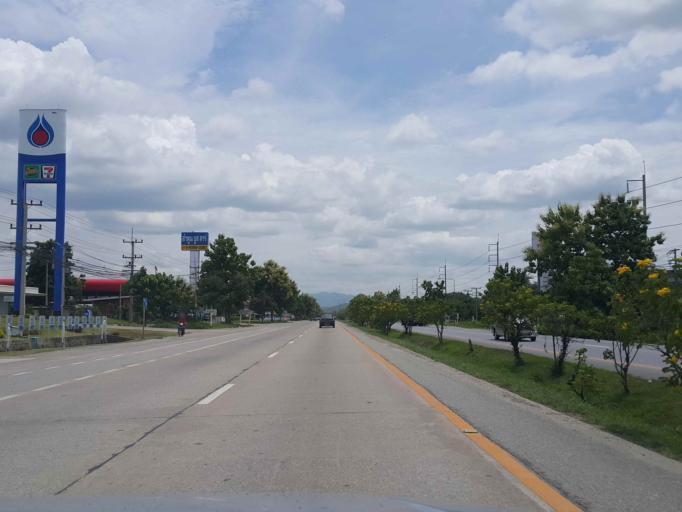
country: TH
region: Lamphun
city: Lamphun
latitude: 18.5714
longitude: 99.0441
